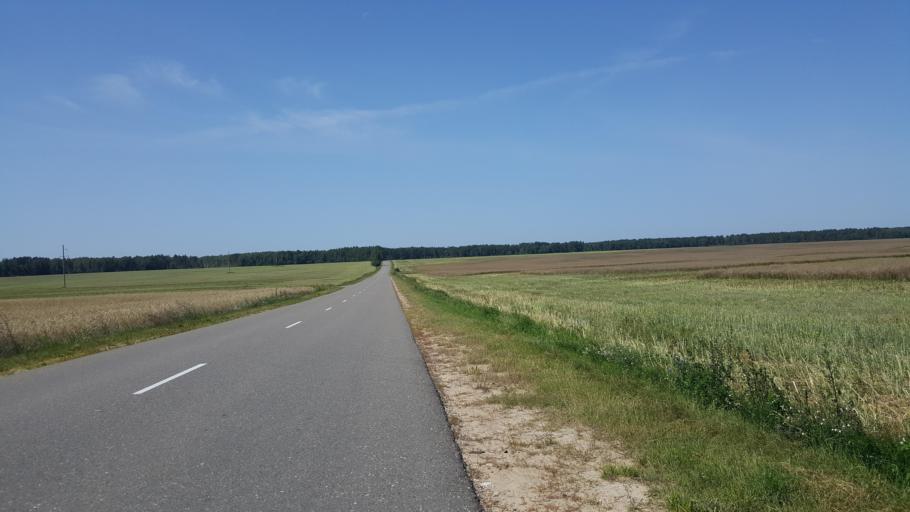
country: BY
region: Brest
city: Kamyanyets
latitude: 52.3855
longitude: 23.7151
